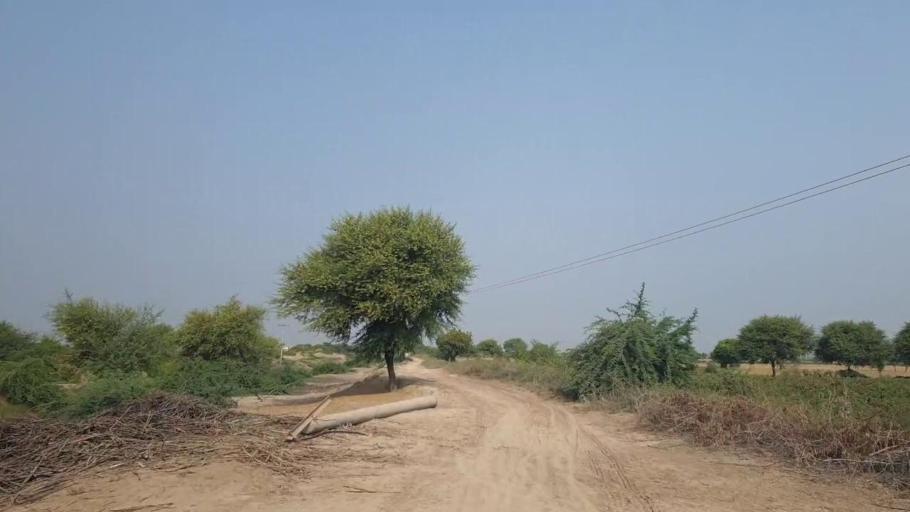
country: PK
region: Sindh
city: Badin
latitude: 24.6999
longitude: 68.7773
